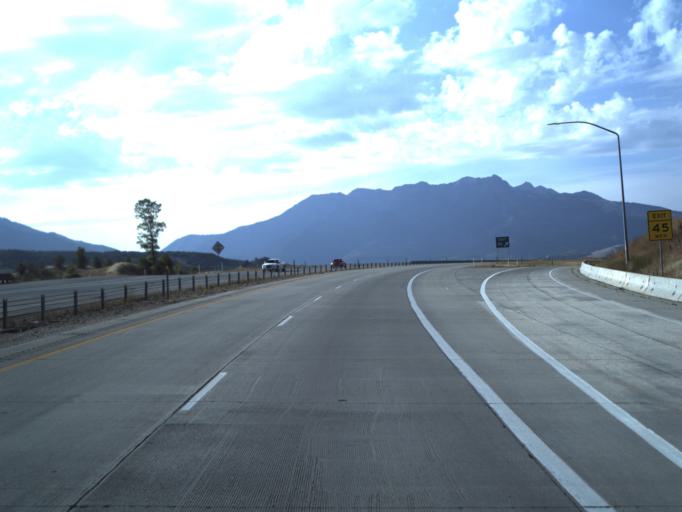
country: US
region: Utah
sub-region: Morgan County
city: Mountain Green
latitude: 41.1129
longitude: -111.7608
